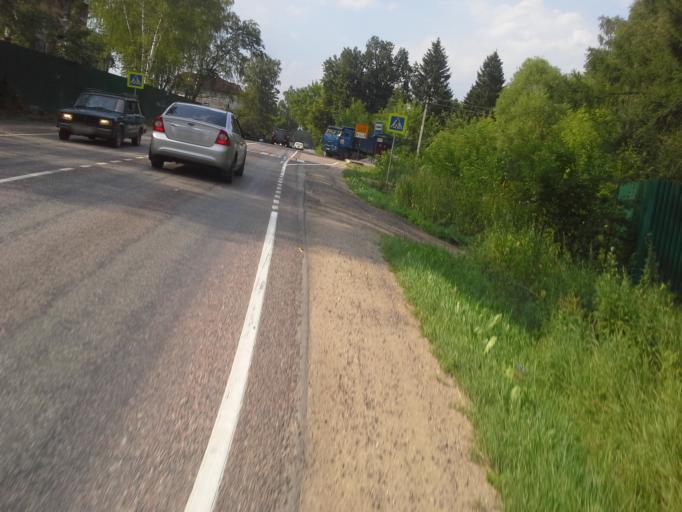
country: RU
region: Moskovskaya
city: Istra
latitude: 55.8875
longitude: 36.7976
